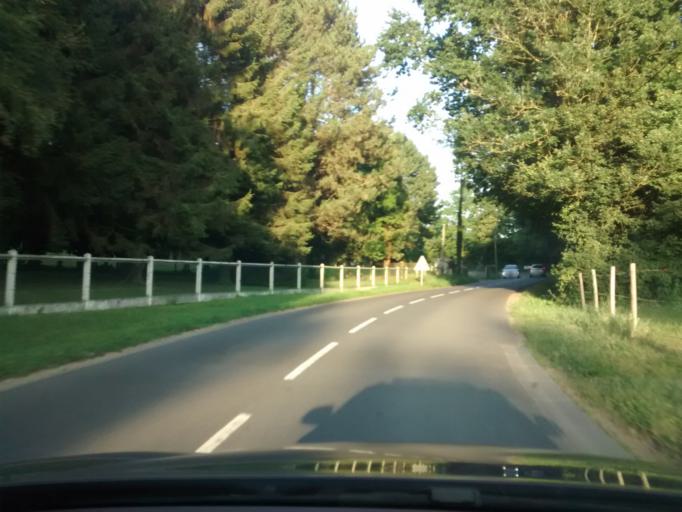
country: FR
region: Lower Normandy
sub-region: Departement du Calvados
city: Blonville-sur-Mer
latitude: 49.3242
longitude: 0.0405
